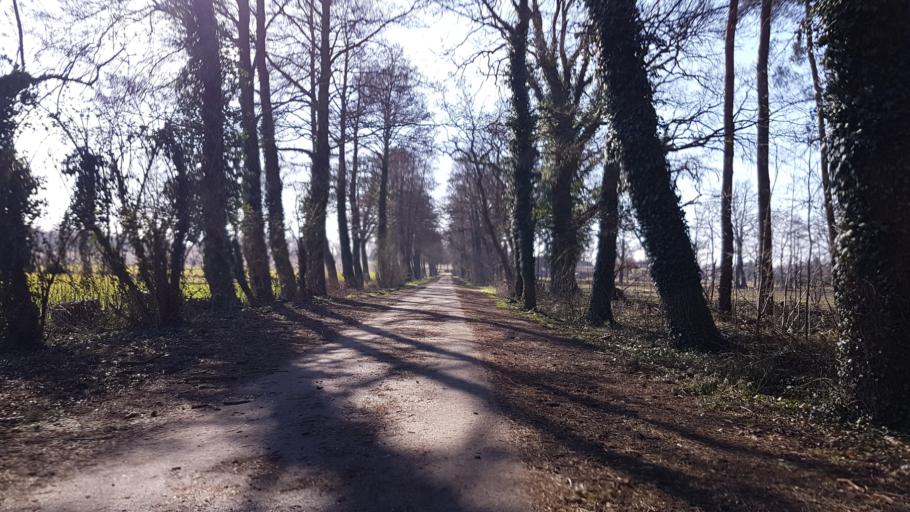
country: DE
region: Lower Saxony
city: Garbsen-Mitte
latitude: 52.4529
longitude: 9.6365
